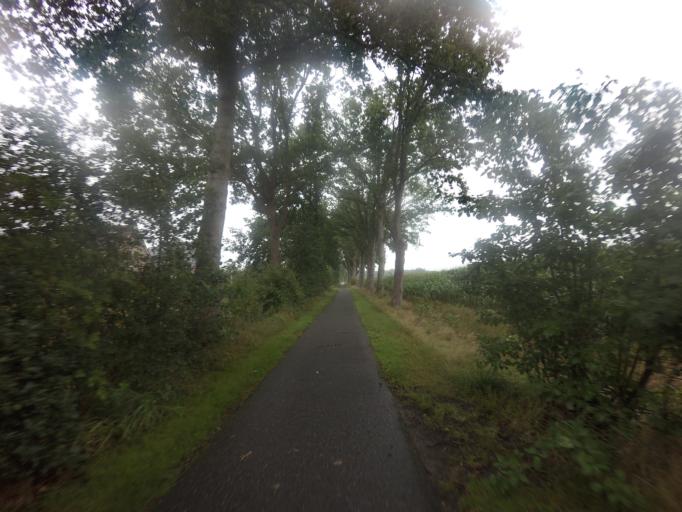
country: NL
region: Friesland
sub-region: Gemeente Heerenveen
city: Nieuwehorne
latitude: 52.9521
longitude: 6.0534
